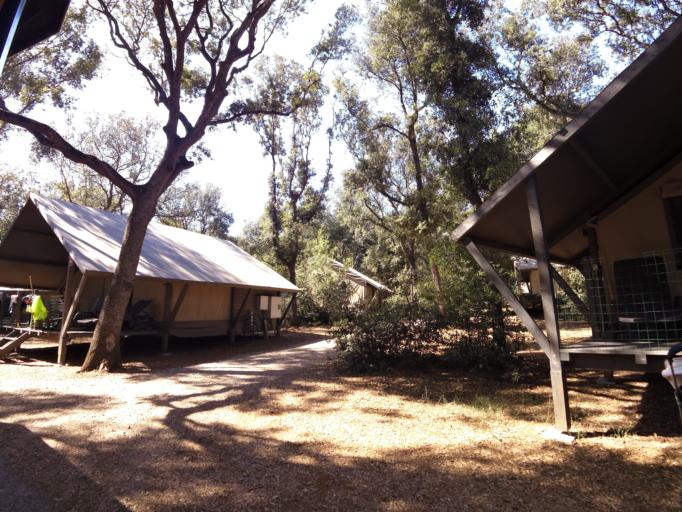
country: IT
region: Tuscany
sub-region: Provincia di Livorno
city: Donoratico
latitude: 43.1535
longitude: 10.5458
